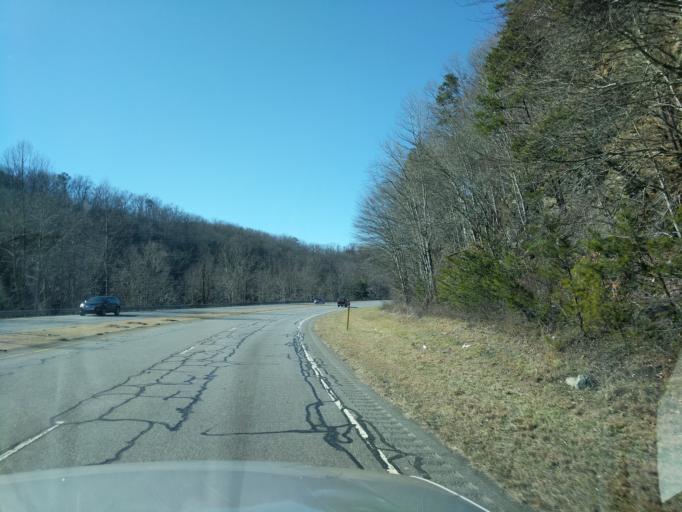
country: US
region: North Carolina
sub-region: Swain County
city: Cherokee
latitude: 35.4039
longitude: -83.3017
